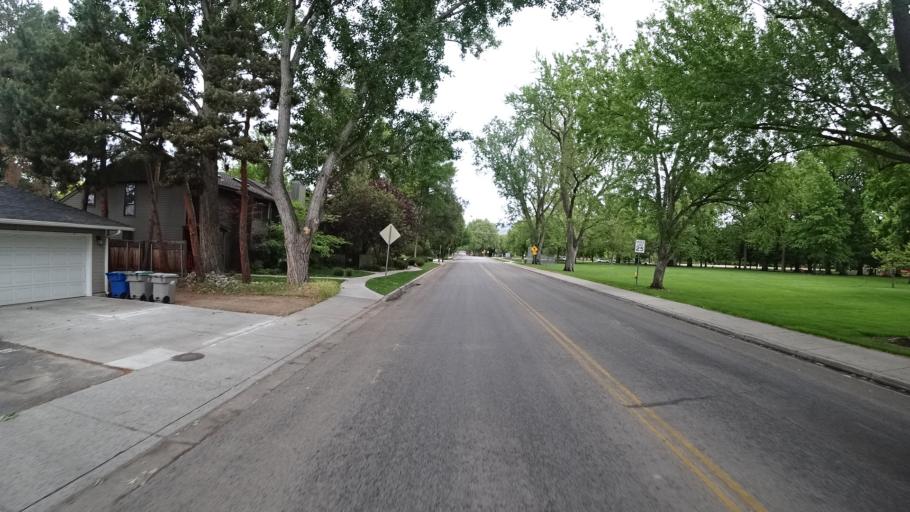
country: US
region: Idaho
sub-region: Ada County
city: Boise
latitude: 43.6030
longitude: -116.1861
